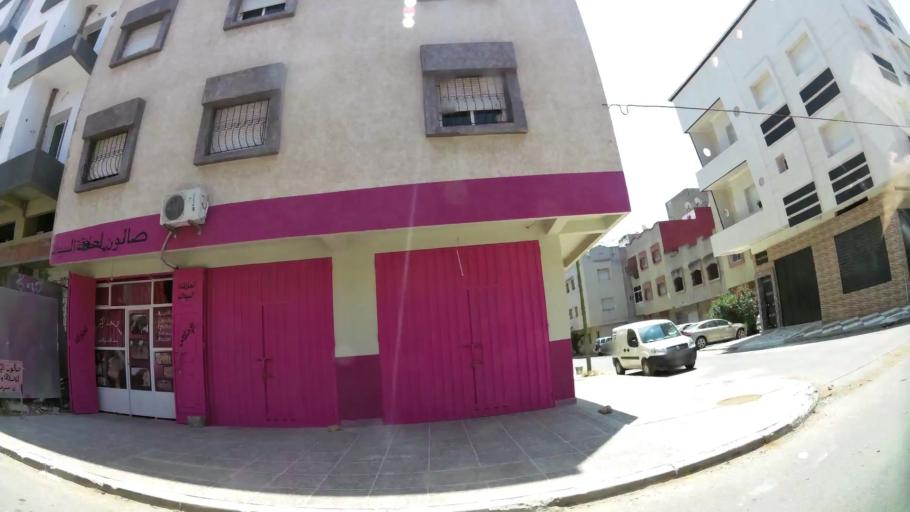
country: MA
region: Gharb-Chrarda-Beni Hssen
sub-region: Kenitra Province
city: Kenitra
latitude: 34.2525
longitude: -6.6119
